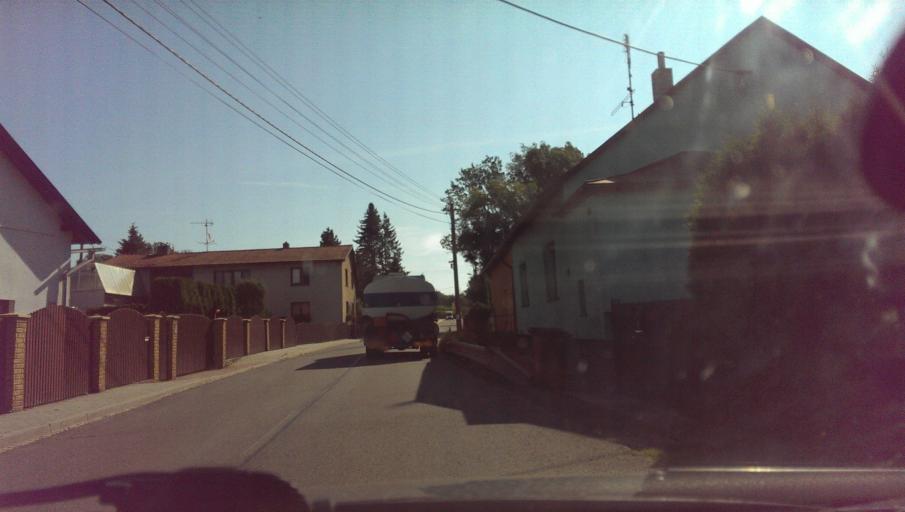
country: CZ
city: Staric
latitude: 49.6838
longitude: 18.2462
